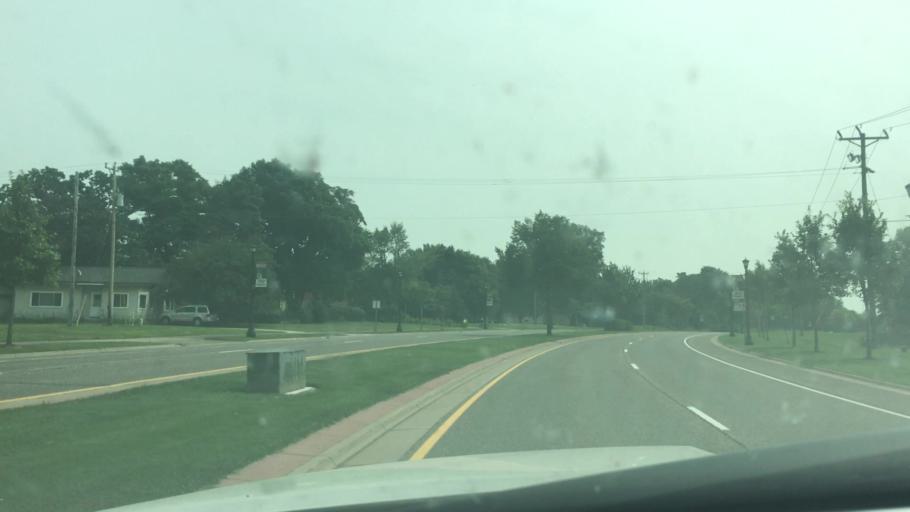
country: US
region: Minnesota
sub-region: Washington County
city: Hugo
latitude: 45.1650
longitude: -93.0059
